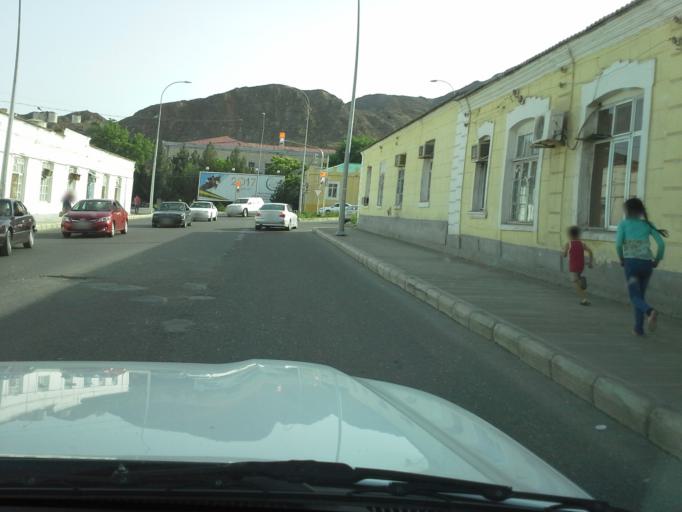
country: TM
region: Balkan
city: Turkmenbasy
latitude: 40.0015
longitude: 52.9890
